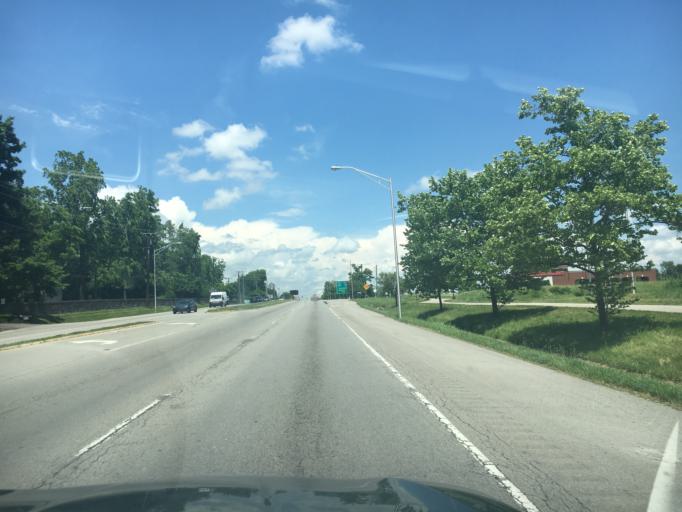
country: US
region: Kentucky
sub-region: Fayette County
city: Lexington-Fayette
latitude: 38.0818
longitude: -84.4920
